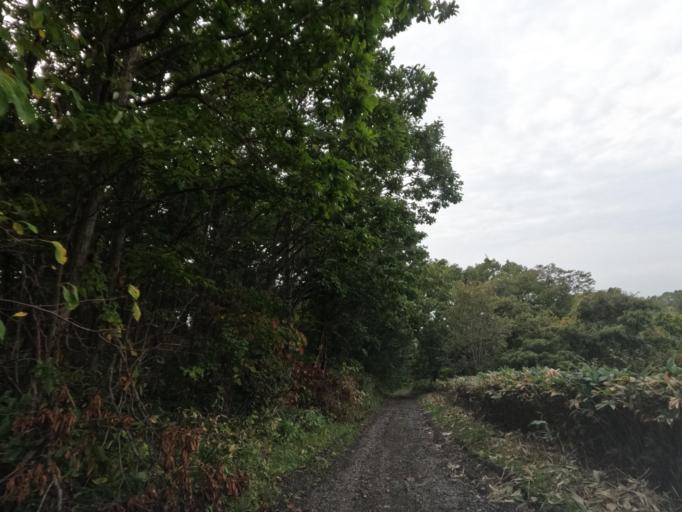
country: JP
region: Hokkaido
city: Date
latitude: 42.4134
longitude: 140.9303
